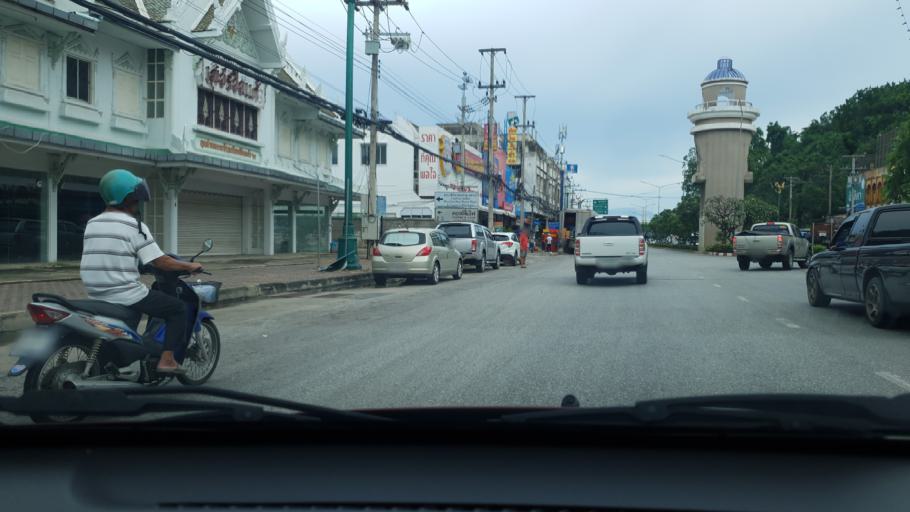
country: TH
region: Phetchaburi
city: Phetchaburi
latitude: 13.1125
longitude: 99.9365
